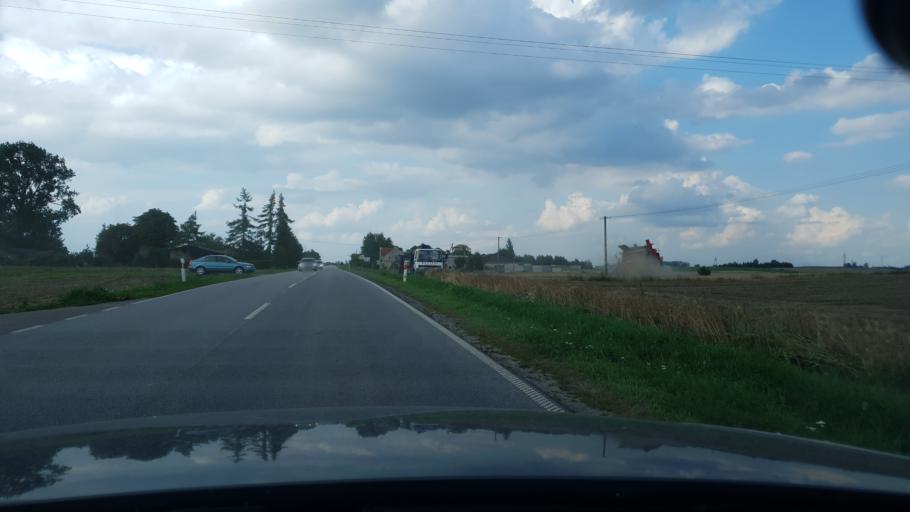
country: PL
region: Kujawsko-Pomorskie
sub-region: Powiat wabrzeski
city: Wabrzezno
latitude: 53.3109
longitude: 18.9350
